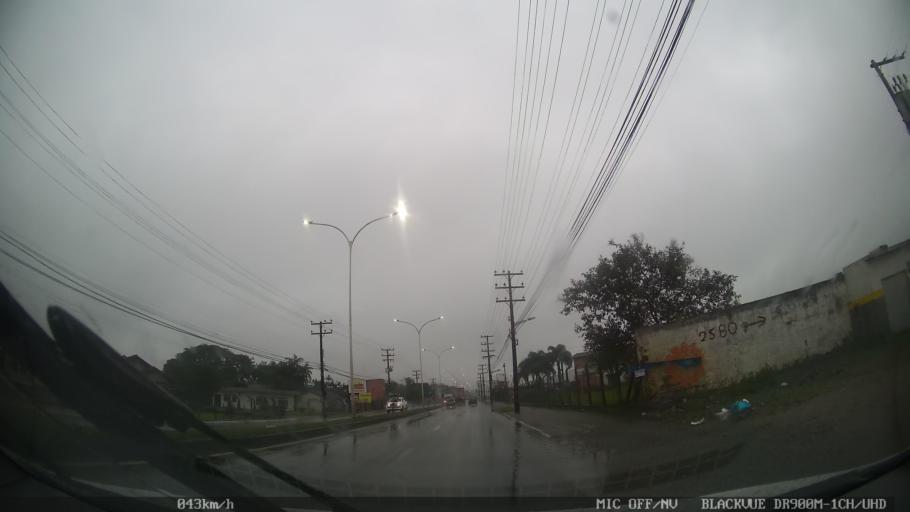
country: BR
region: Santa Catarina
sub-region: Itajai
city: Itajai
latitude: -26.8890
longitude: -48.7084
